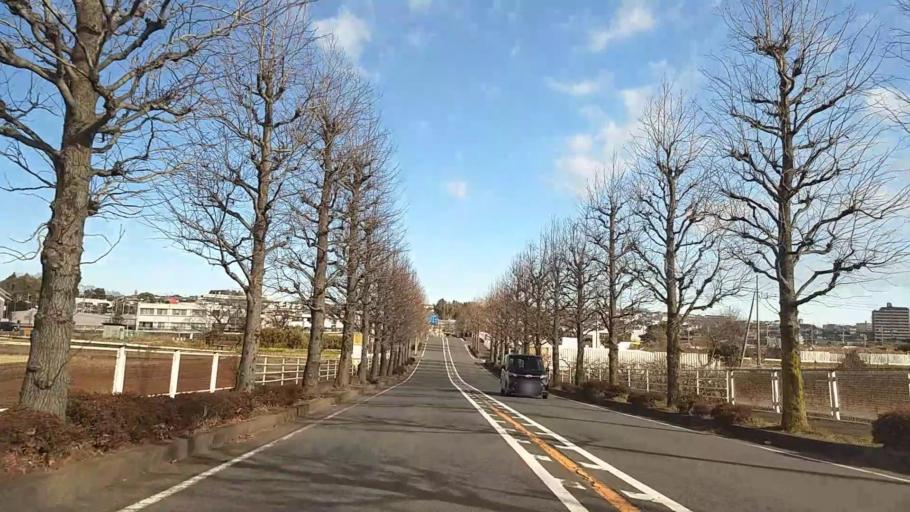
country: JP
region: Kanagawa
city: Atsugi
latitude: 35.4287
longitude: 139.3287
